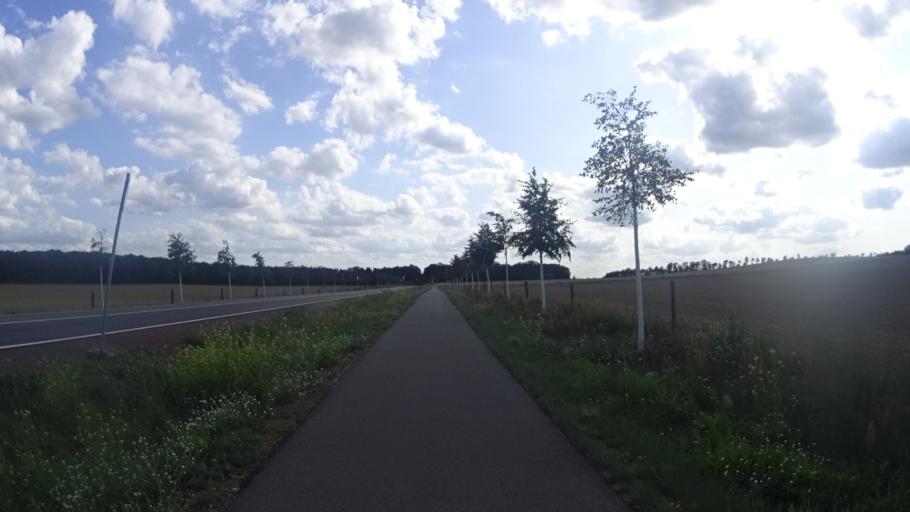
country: DE
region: Brandenburg
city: Rhinow
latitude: 52.6953
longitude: 12.3666
